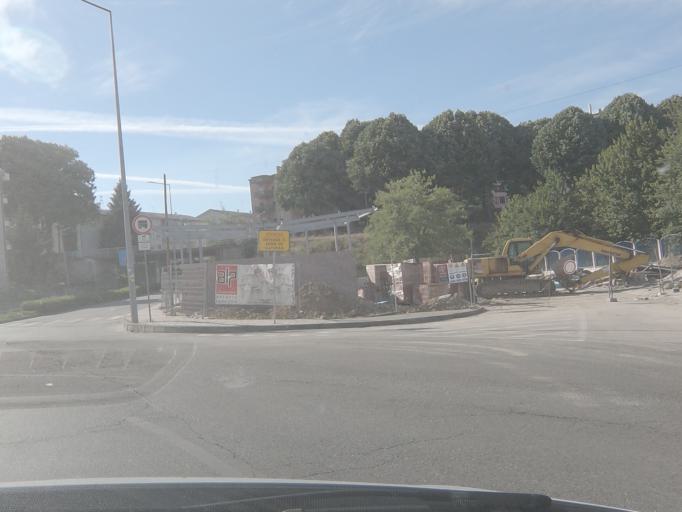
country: PT
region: Viseu
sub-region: Viseu
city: Viseu
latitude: 40.6495
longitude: -7.9091
